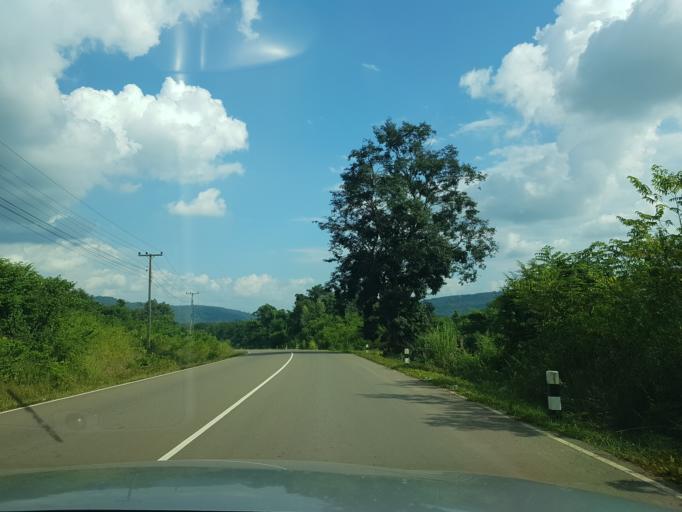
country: TH
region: Nong Khai
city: Sangkhom
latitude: 18.0337
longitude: 102.3670
